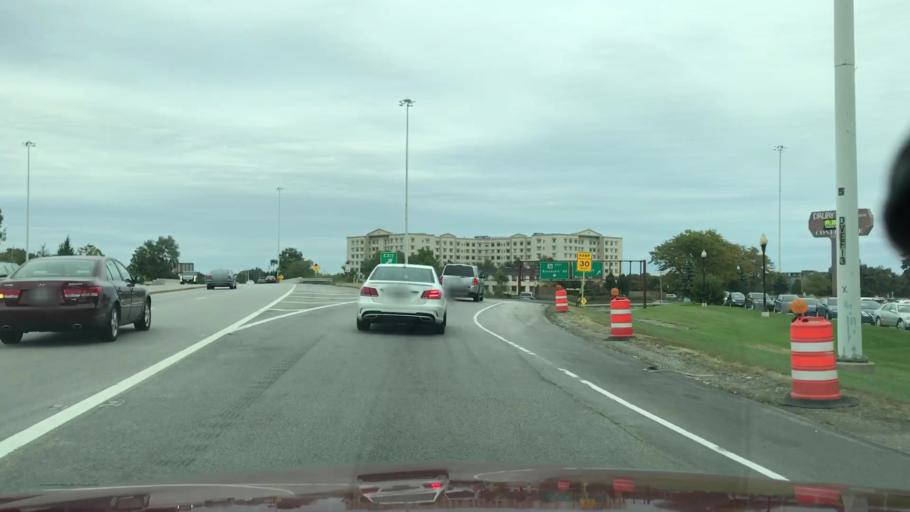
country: US
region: Illinois
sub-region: DuPage County
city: Oakbrook Terrace
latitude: 41.8597
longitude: -87.9547
